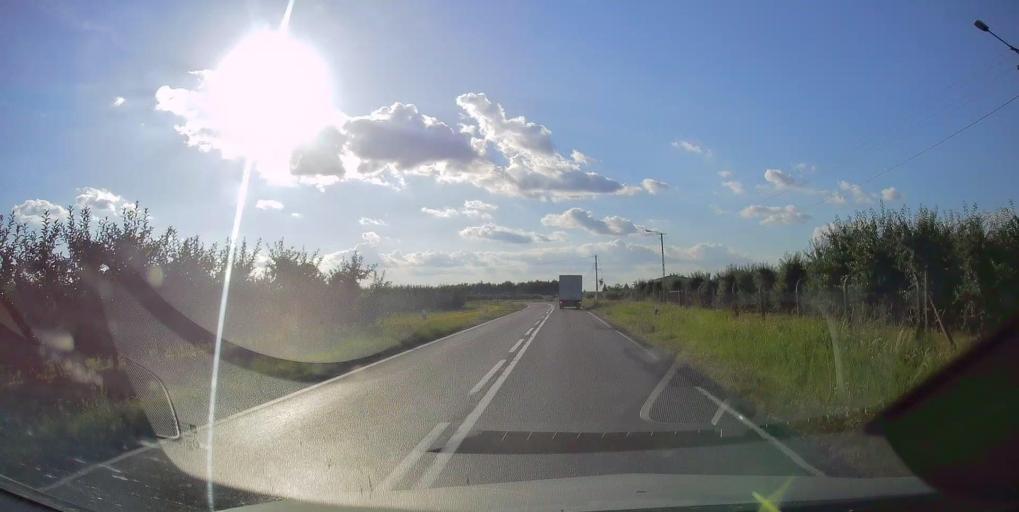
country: PL
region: Masovian Voivodeship
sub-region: Powiat grojecki
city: Bledow
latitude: 51.8099
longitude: 20.6794
